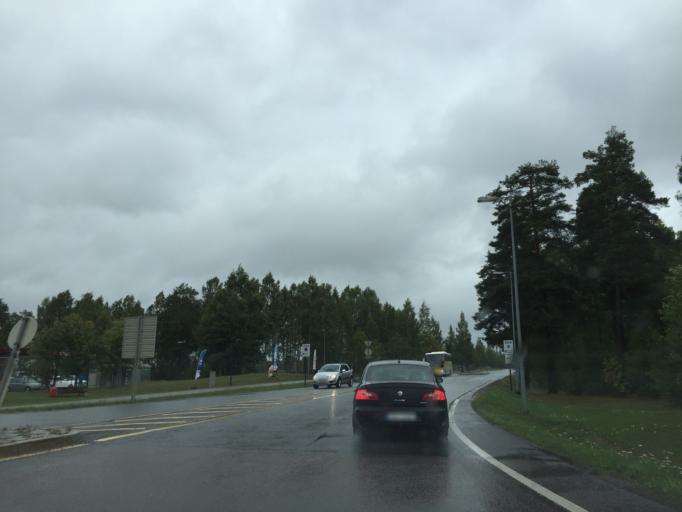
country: NO
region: Akershus
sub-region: Nannestad
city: Teigebyen
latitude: 60.1786
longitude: 11.0819
